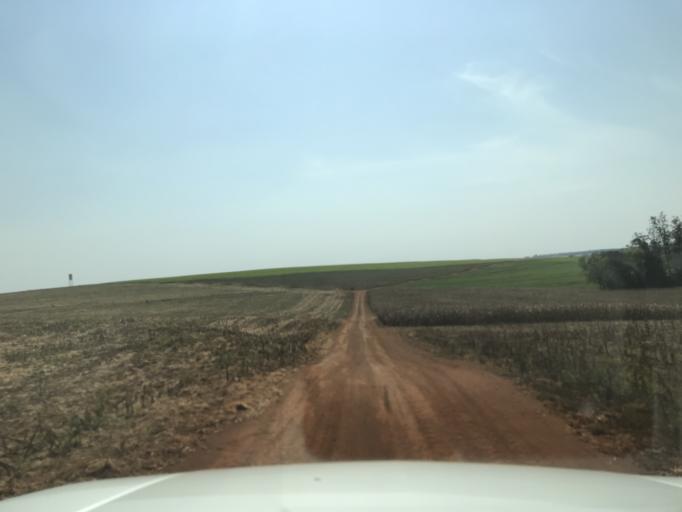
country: BR
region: Parana
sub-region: Palotina
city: Palotina
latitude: -24.2321
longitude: -53.7460
